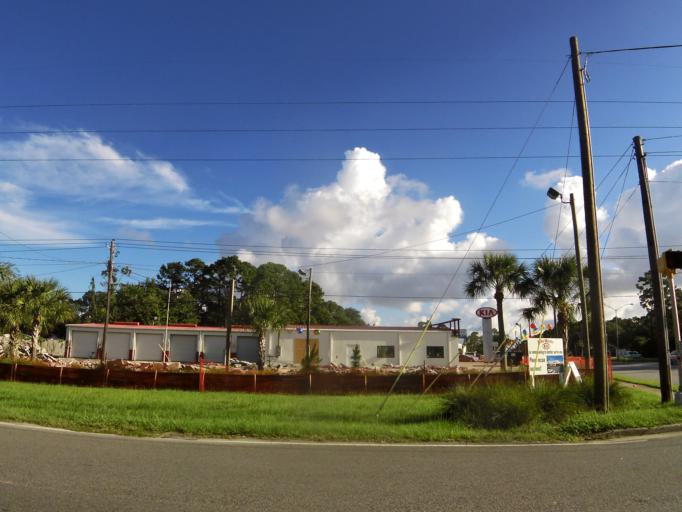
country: US
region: Georgia
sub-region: Glynn County
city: Country Club Estates
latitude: 31.2257
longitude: -81.4772
